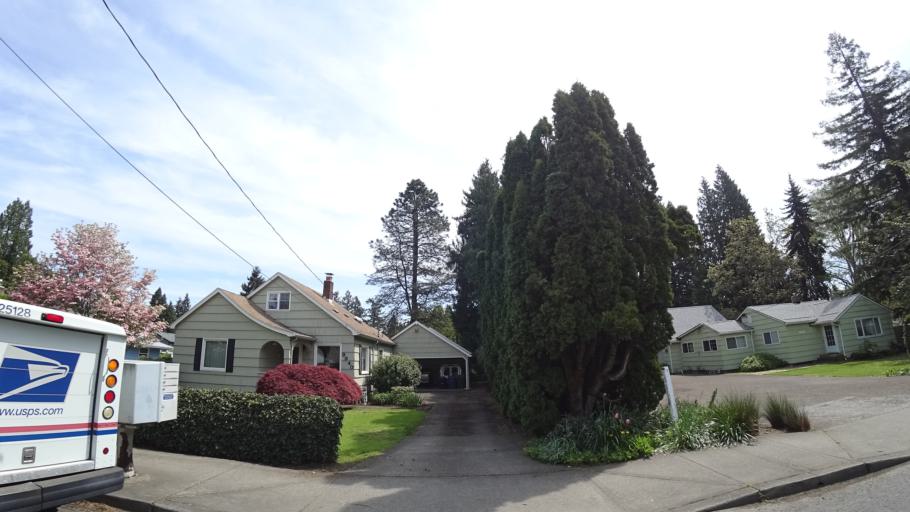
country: US
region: Oregon
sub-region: Clackamas County
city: Milwaukie
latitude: 45.4505
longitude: -122.6046
